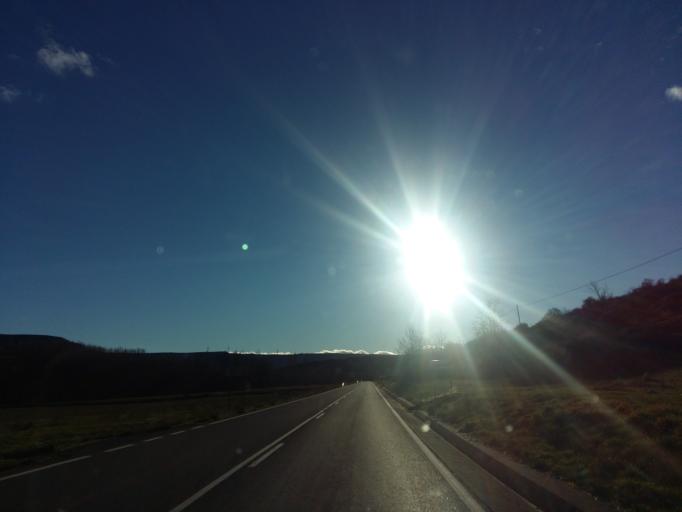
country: ES
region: Cantabria
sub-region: Provincia de Cantabria
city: San Martin de Elines
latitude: 42.8286
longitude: -3.9039
